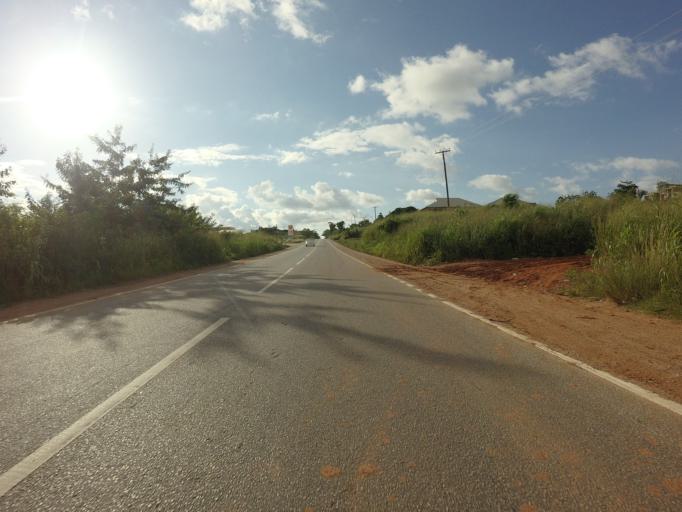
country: GH
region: Ashanti
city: Tafo
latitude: 6.8863
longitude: -1.6457
